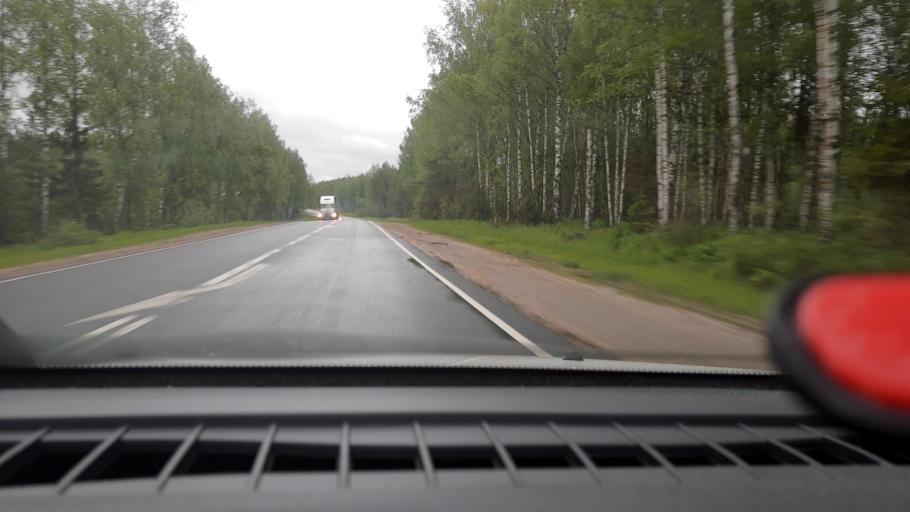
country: RU
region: Nizjnij Novgorod
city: Krasnyye Baki
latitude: 57.0510
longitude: 45.1358
